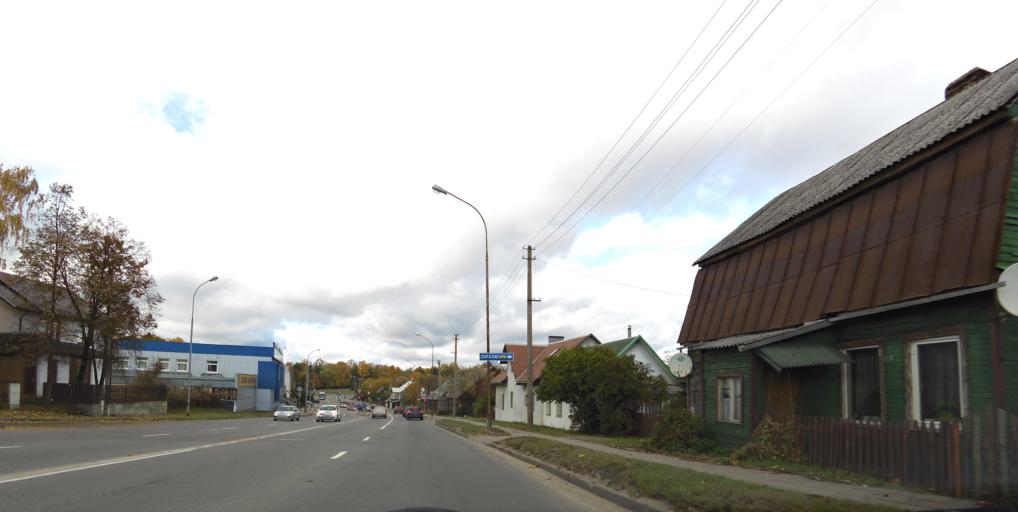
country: LT
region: Vilnius County
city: Rasos
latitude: 54.6612
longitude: 25.3028
